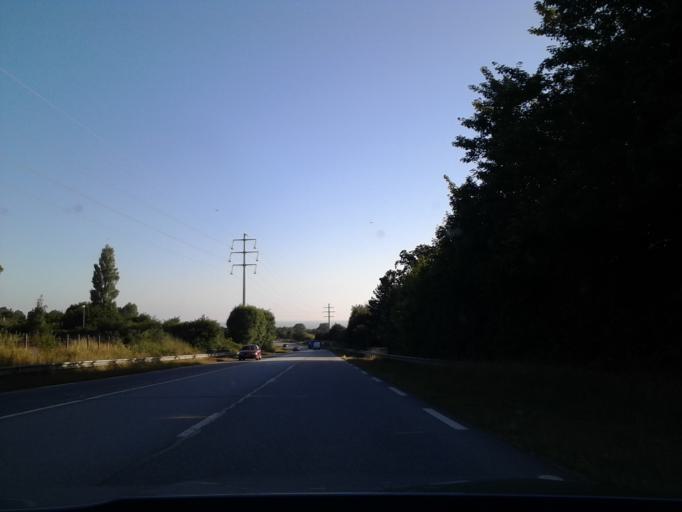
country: FR
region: Lower Normandy
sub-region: Departement de la Manche
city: La Glacerie
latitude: 49.6192
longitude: -1.5819
